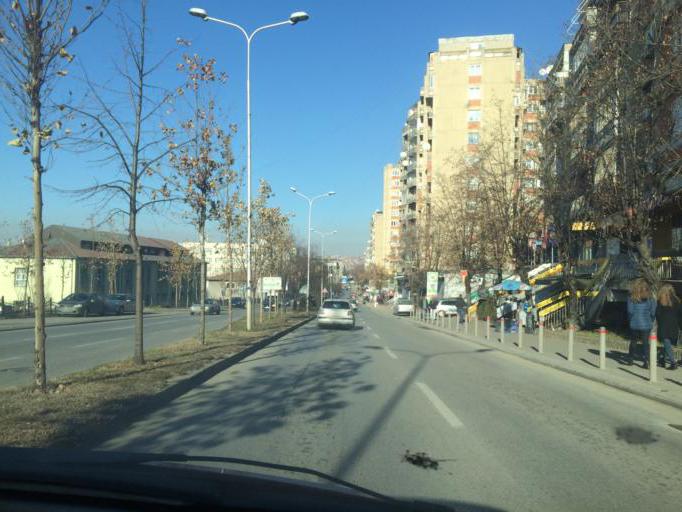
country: XK
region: Pristina
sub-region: Komuna e Prishtines
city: Pristina
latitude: 42.6554
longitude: 21.1642
